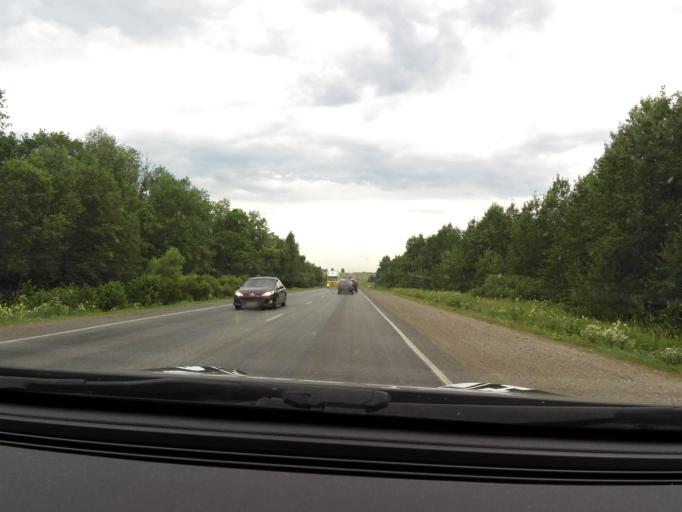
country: RU
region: Bashkortostan
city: Kudeyevskiy
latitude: 54.8171
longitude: 56.7813
